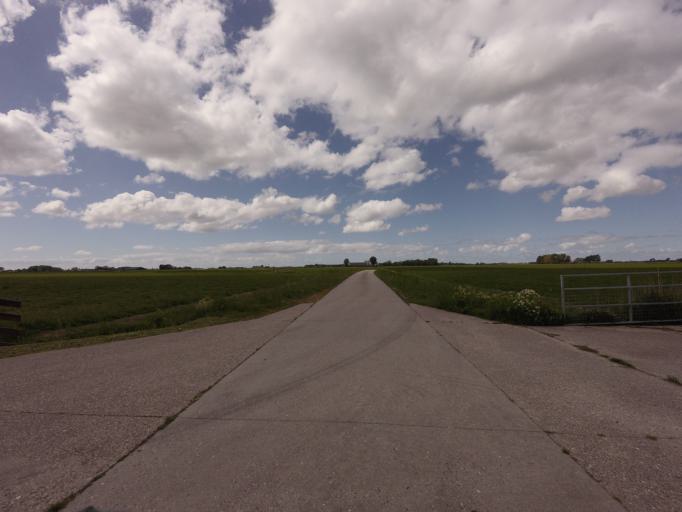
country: NL
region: Friesland
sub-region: Gemeente Franekeradeel
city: Tzum
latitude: 53.1291
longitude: 5.5619
